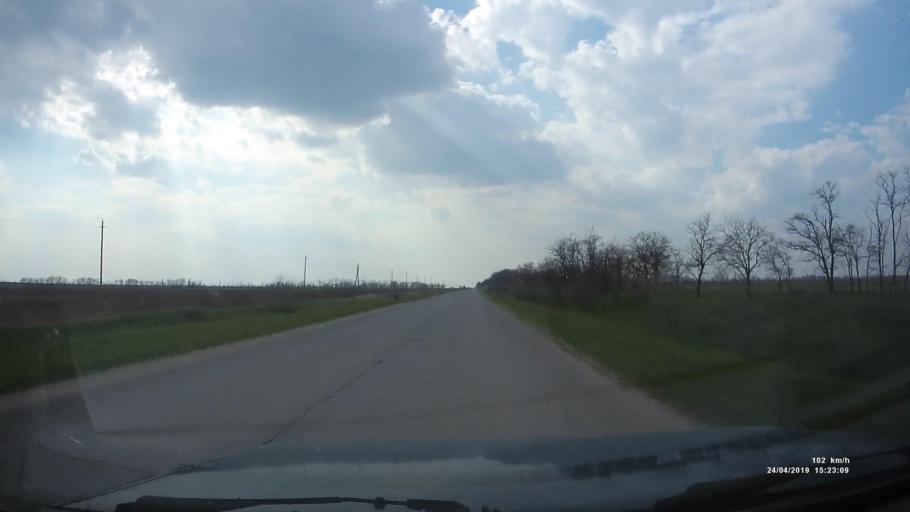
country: RU
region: Rostov
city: Remontnoye
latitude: 46.5420
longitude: 43.0958
